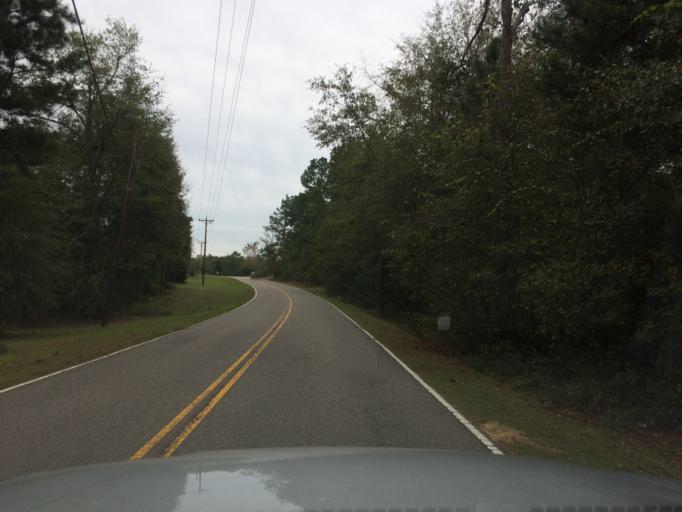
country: US
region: South Carolina
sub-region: Aiken County
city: New Ellenton
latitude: 33.4142
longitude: -81.6975
